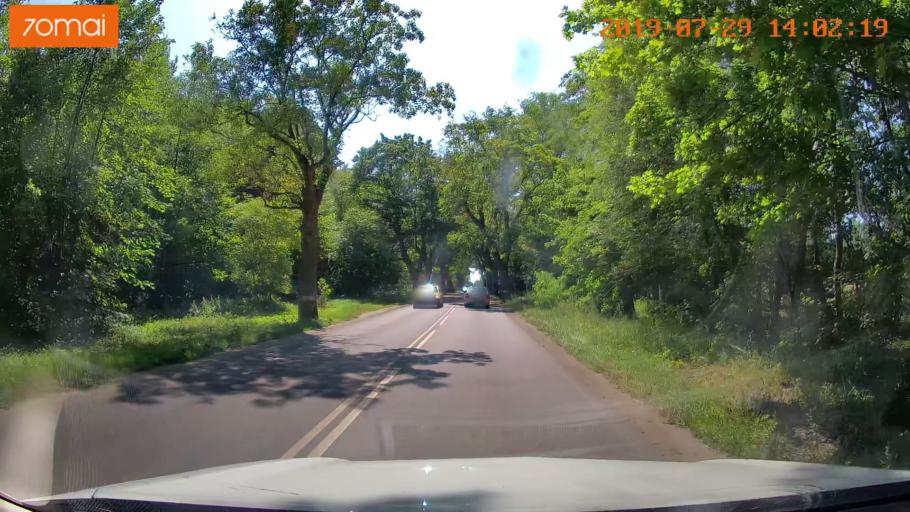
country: RU
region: Kaliningrad
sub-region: Gorod Kaliningrad
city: Baltiysk
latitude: 54.6638
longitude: 19.9165
